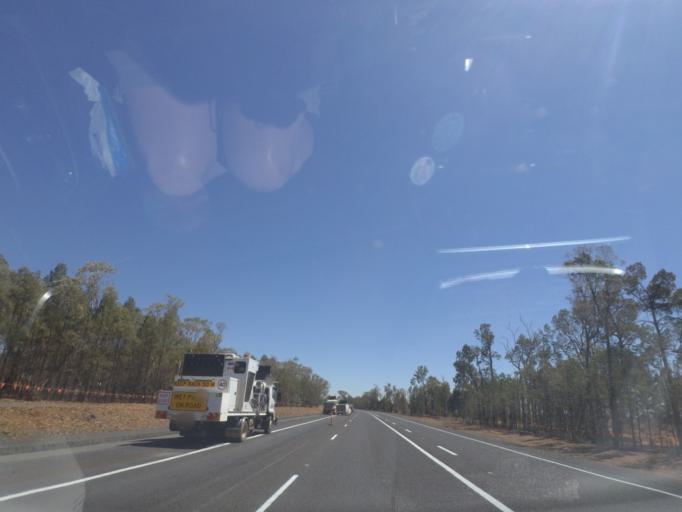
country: AU
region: New South Wales
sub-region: Gilgandra
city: Gilgandra
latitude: -31.6636
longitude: 148.7202
